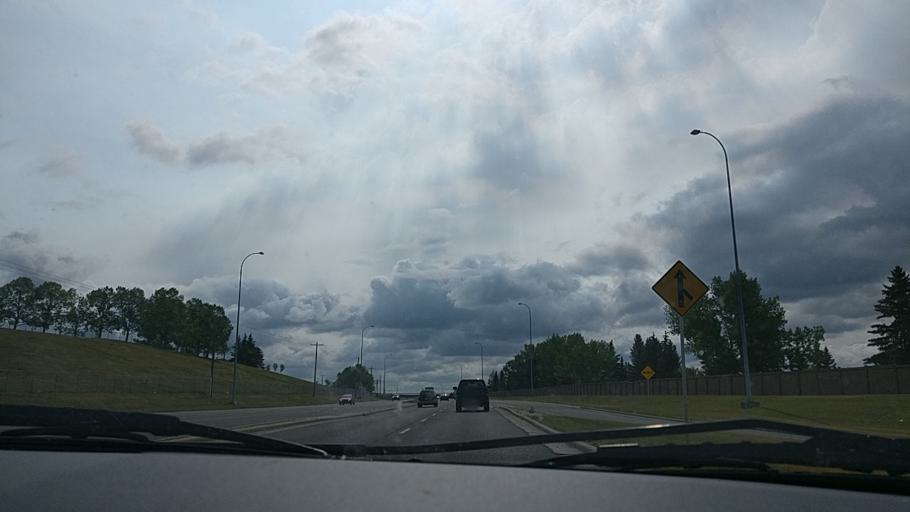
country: CA
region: Alberta
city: Calgary
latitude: 51.1149
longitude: -114.1542
